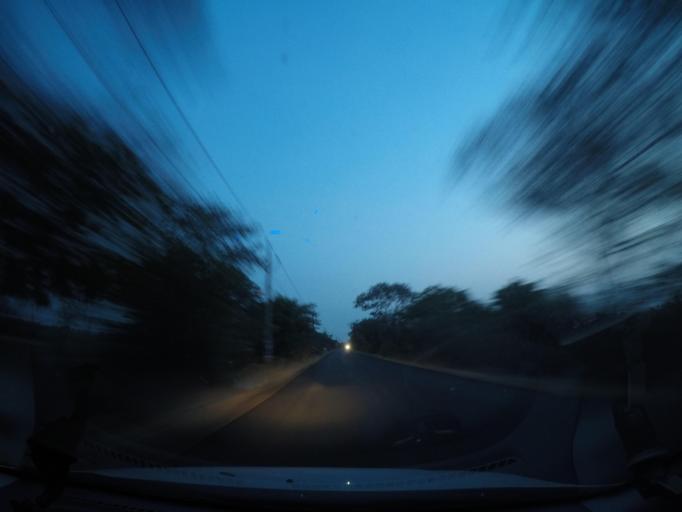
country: IN
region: Andhra Pradesh
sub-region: West Godavari
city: Tadepallegudem
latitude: 16.7728
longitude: 81.4237
